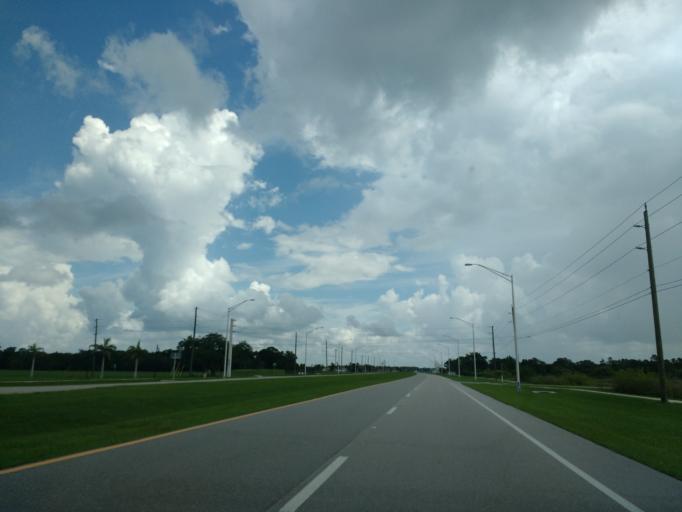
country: US
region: Florida
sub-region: Lee County
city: Burnt Store Marina
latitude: 26.7813
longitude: -82.0379
